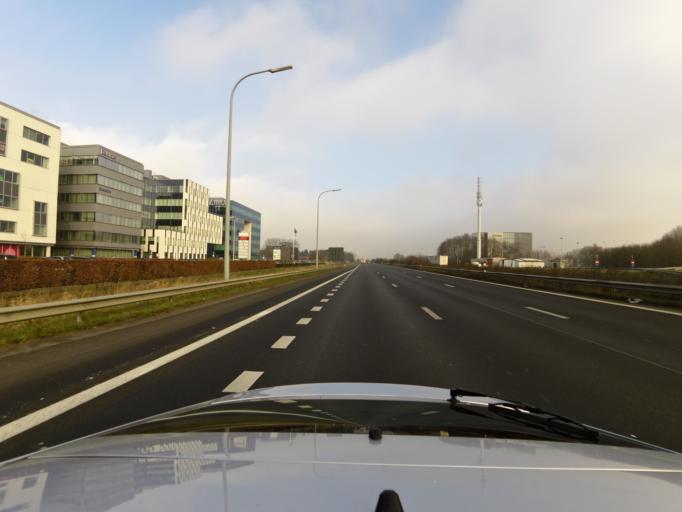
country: BE
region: Flanders
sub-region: Provincie West-Vlaanderen
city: Izegem
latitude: 50.9196
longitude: 3.1761
